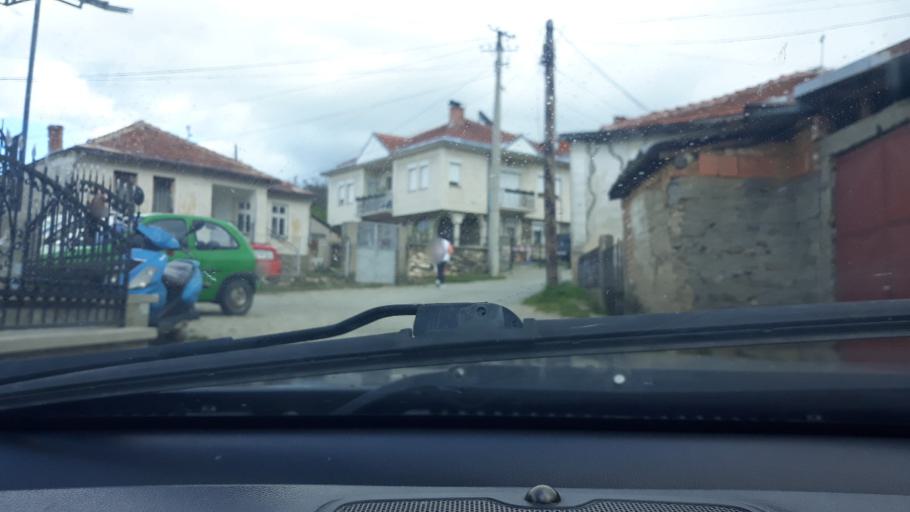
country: MK
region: Krusevo
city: Krushevo
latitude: 41.3666
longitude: 21.2530
